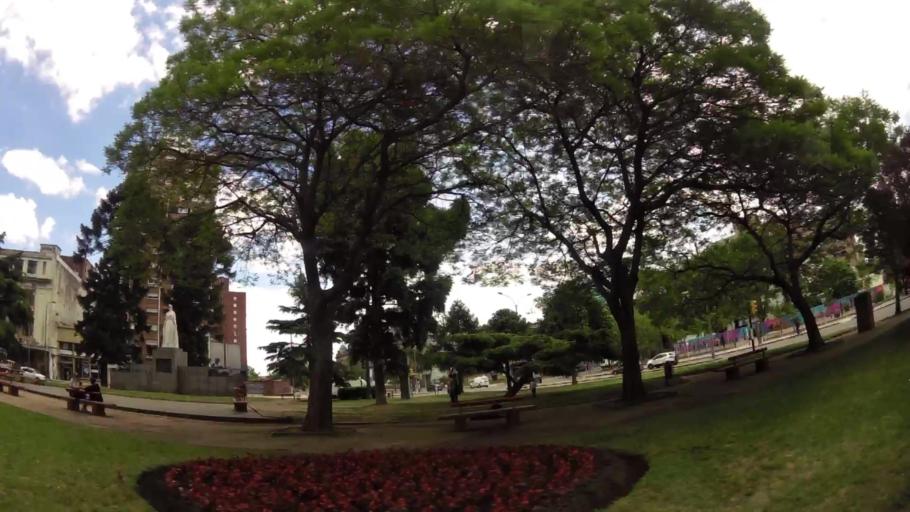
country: UY
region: Montevideo
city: Montevideo
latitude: -34.8996
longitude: -56.1915
